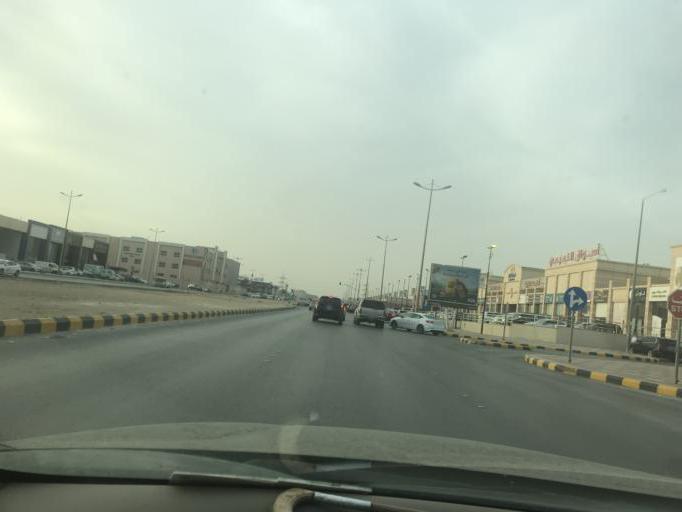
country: SA
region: Ar Riyad
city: Riyadh
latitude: 24.8060
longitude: 46.7374
